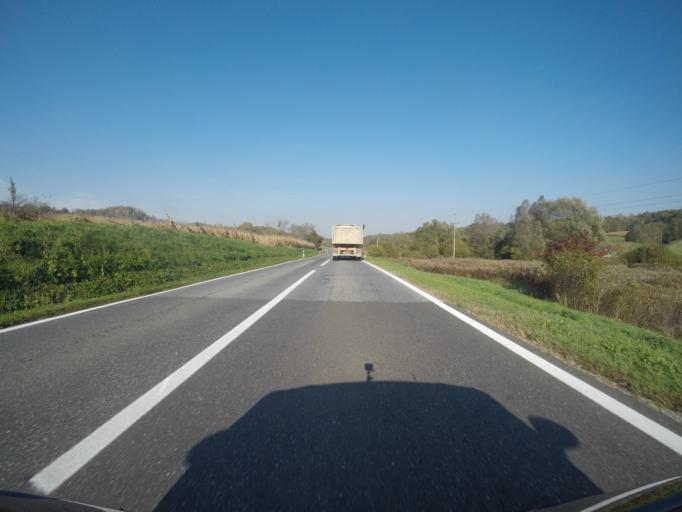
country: HR
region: Koprivnicko-Krizevacka
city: Virje
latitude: 45.9980
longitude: 16.9175
